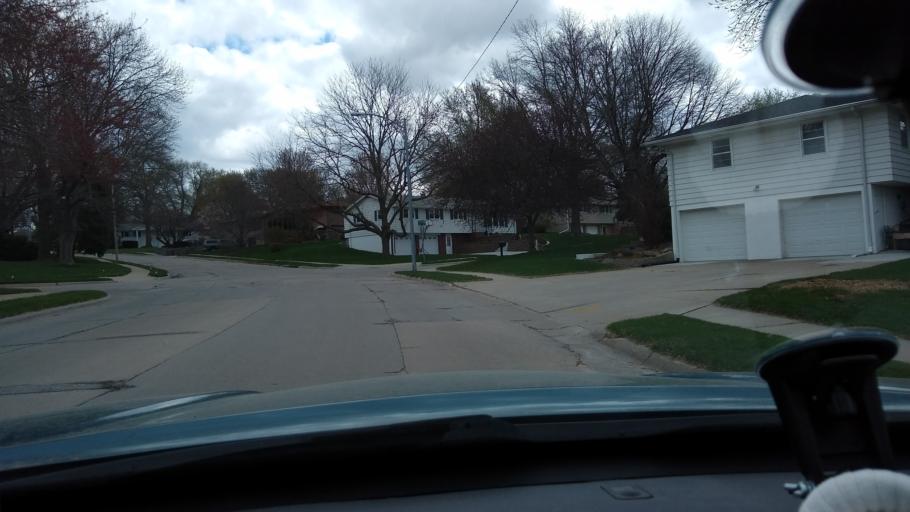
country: US
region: Nebraska
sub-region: Douglas County
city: Ralston
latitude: 41.2273
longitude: -96.0937
